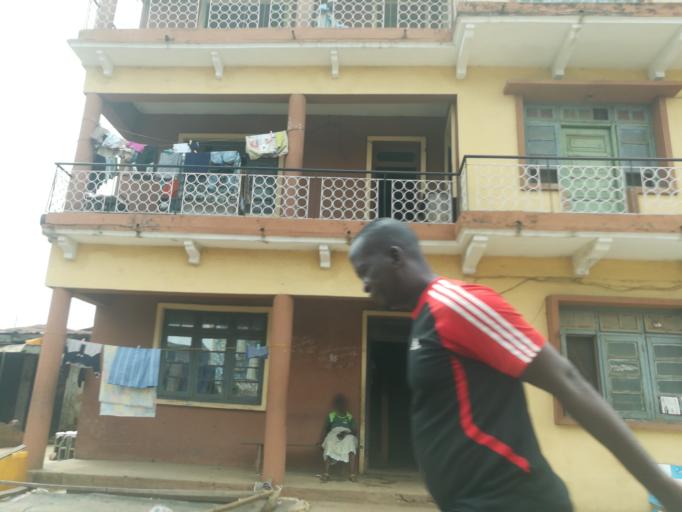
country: NG
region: Lagos
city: Ikorodu
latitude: 6.6140
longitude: 3.5099
